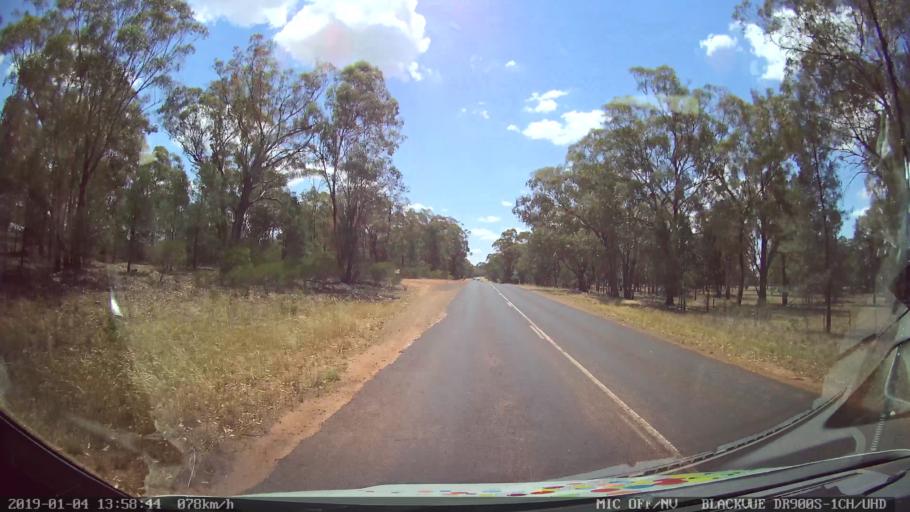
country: AU
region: New South Wales
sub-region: Dubbo Municipality
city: Dubbo
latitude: -32.3252
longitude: 148.5938
